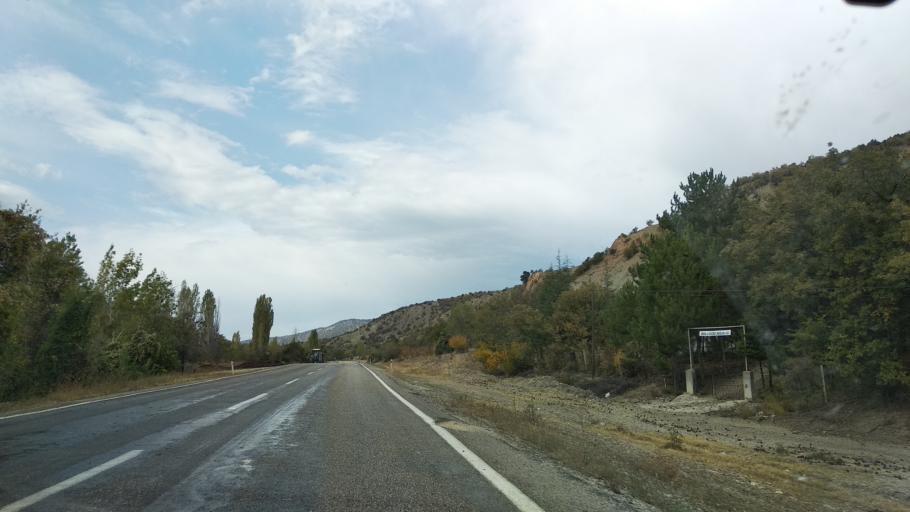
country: TR
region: Ankara
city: Nallihan
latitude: 40.3072
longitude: 31.2924
